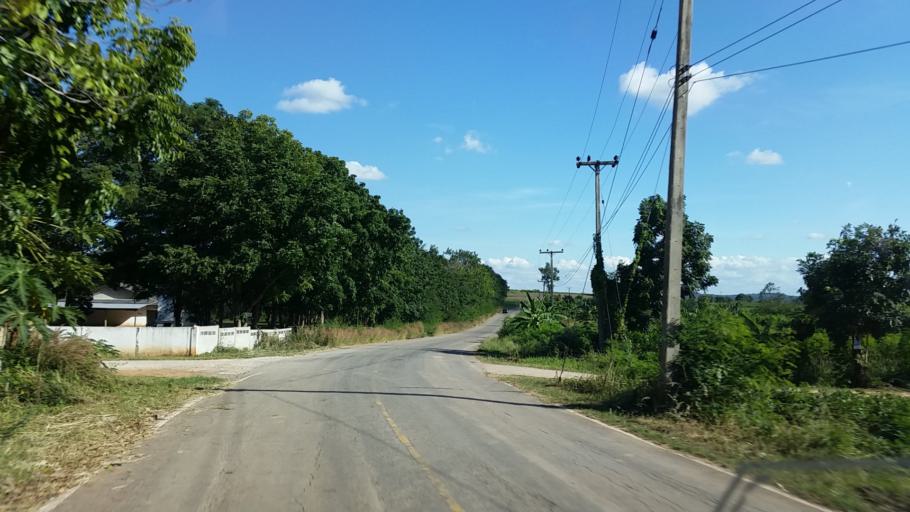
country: TH
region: Chaiyaphum
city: Thep Sathit
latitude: 15.5557
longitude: 101.4457
